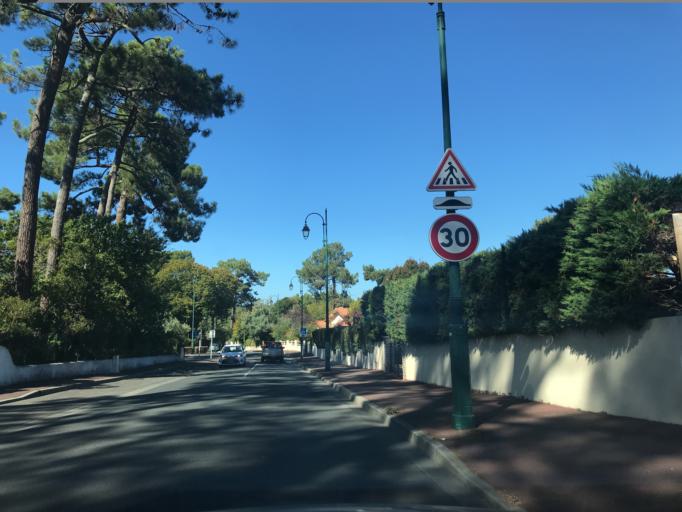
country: FR
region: Aquitaine
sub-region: Departement de la Gironde
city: Arcachon
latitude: 44.6506
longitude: -1.1795
